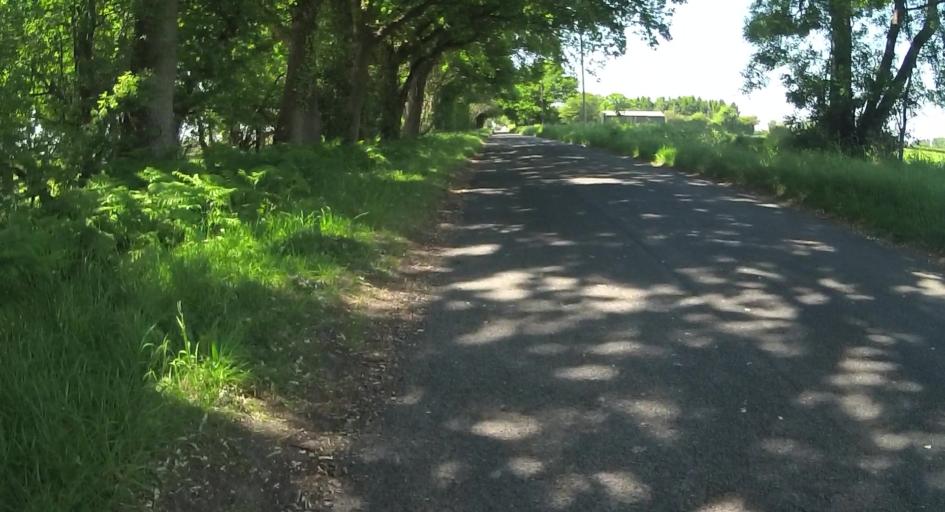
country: GB
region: England
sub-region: Hampshire
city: Kingsclere
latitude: 51.3430
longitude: -1.1975
